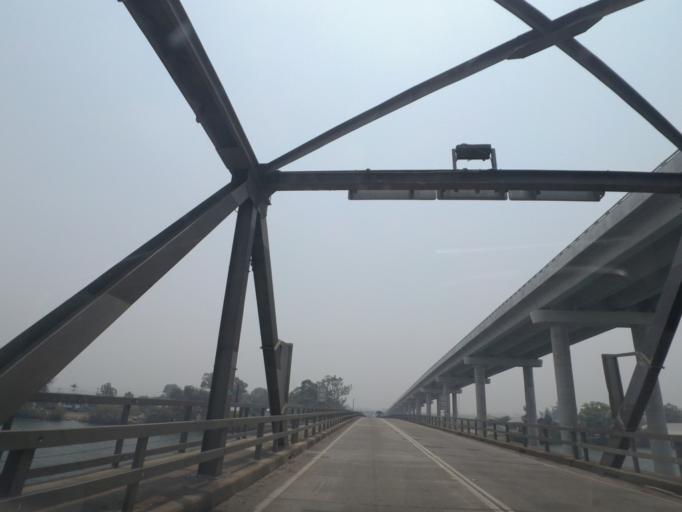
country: AU
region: New South Wales
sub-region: Clarence Valley
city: Maclean
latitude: -29.4299
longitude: 153.2407
